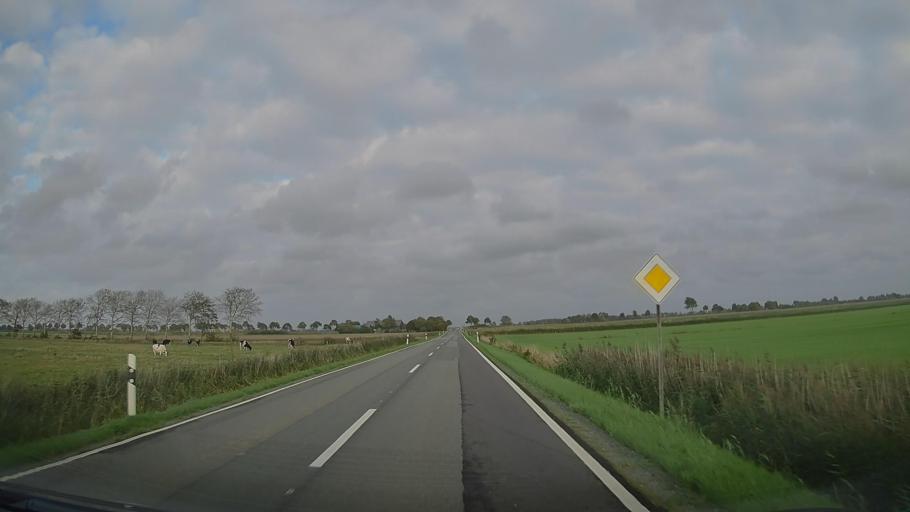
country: DE
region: Schleswig-Holstein
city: Husum
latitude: 54.4392
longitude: 9.0365
